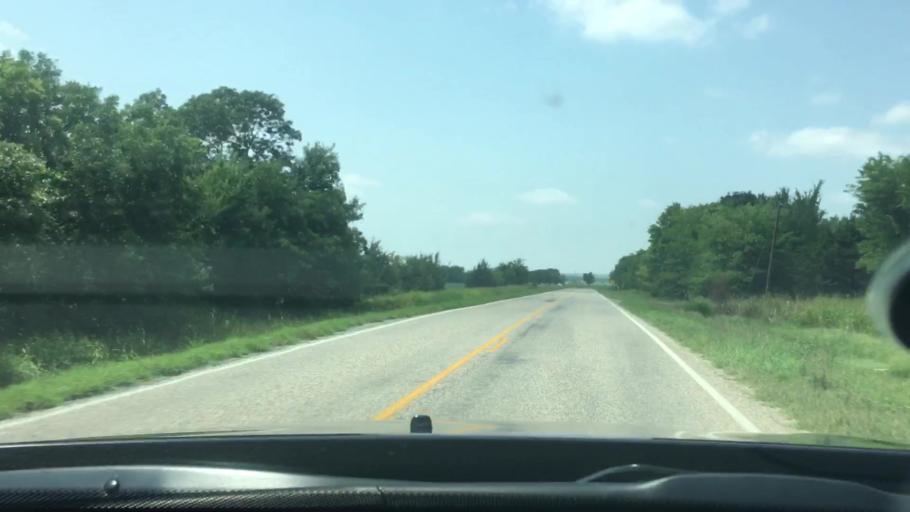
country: US
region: Oklahoma
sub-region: Johnston County
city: Tishomingo
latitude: 34.3735
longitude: -96.4613
